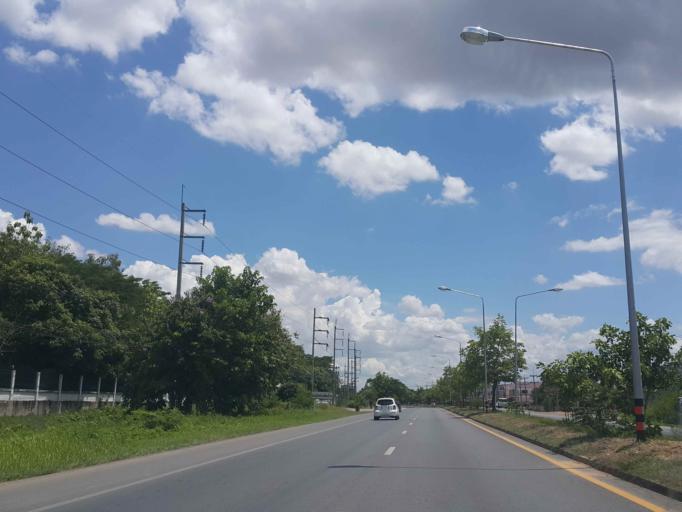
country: TH
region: Phrae
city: Nong Muang Khai
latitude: 18.2355
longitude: 100.2144
